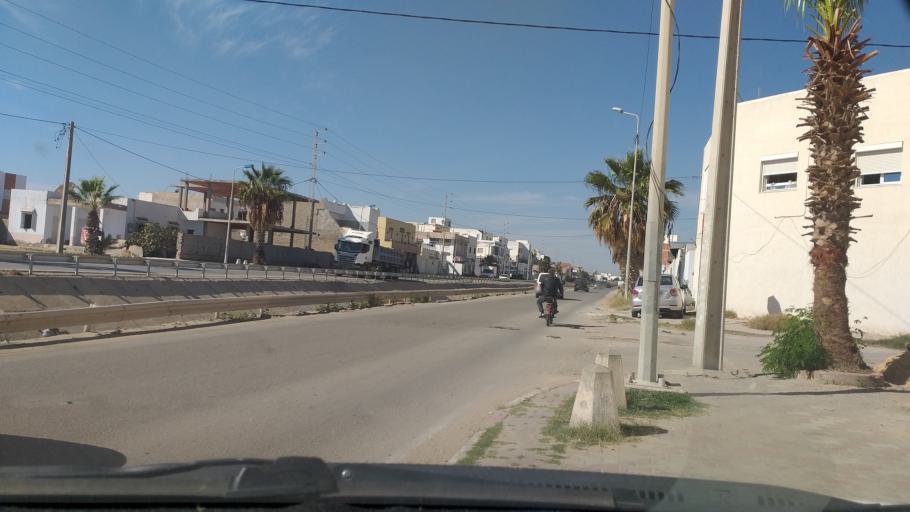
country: TN
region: Safaqis
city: Al Qarmadah
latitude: 34.7693
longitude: 10.7725
